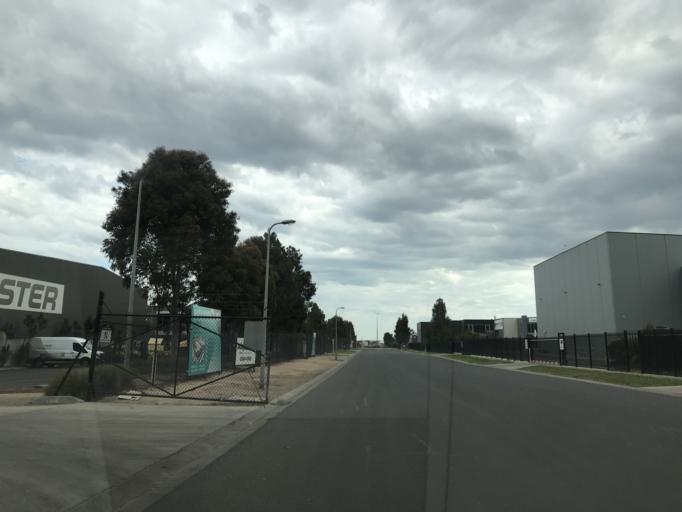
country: AU
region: Victoria
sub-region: Wyndham
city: Truganina
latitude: -37.8192
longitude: 144.7451
